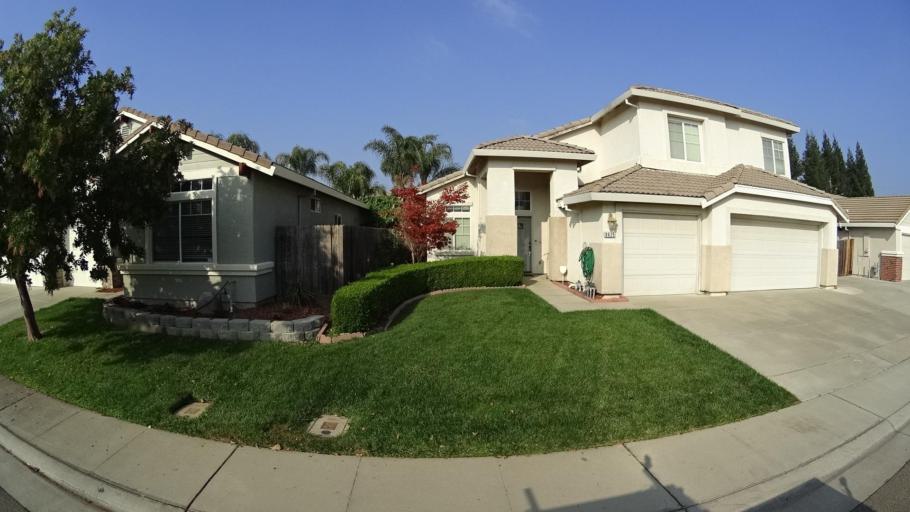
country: US
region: California
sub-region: Sacramento County
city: Elk Grove
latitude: 38.4131
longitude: -121.3381
